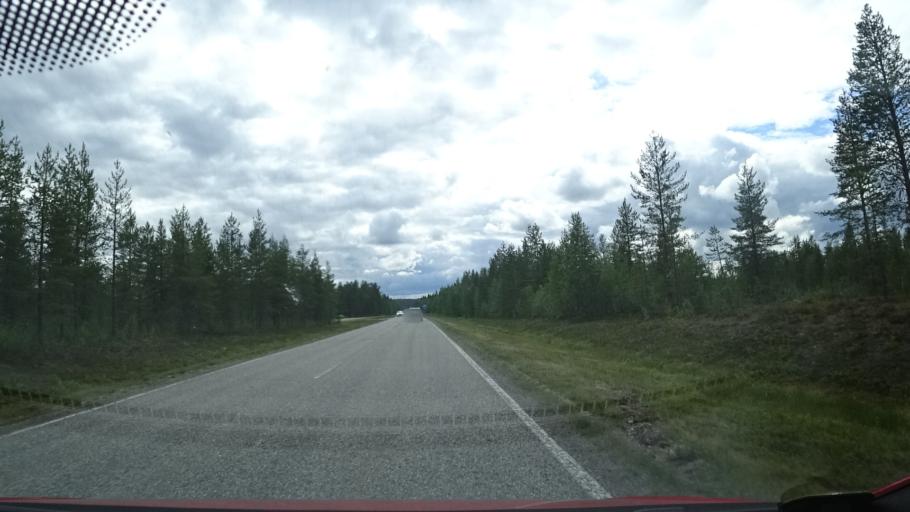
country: FI
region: Lapland
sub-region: Tunturi-Lappi
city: Kittilae
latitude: 67.4541
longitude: 24.9462
